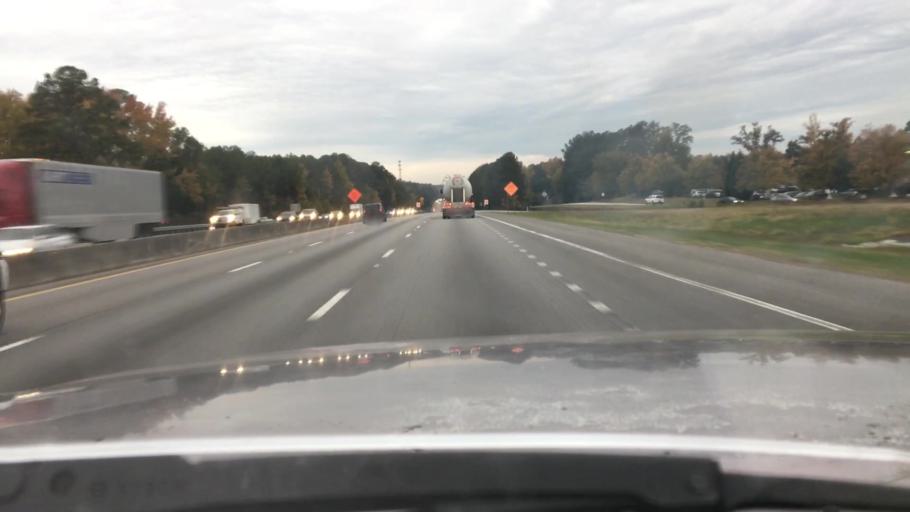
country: US
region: South Carolina
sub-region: Lexington County
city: Oak Grove
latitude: 34.0107
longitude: -81.1506
